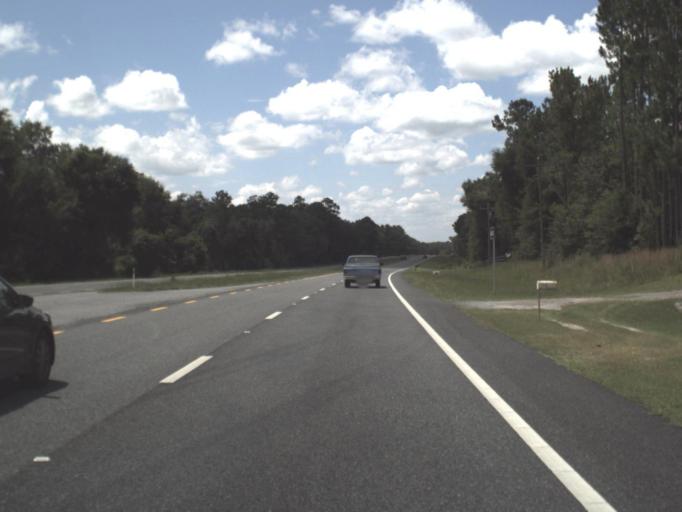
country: US
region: Florida
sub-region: Jefferson County
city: Monticello
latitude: 30.3375
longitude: -83.7824
